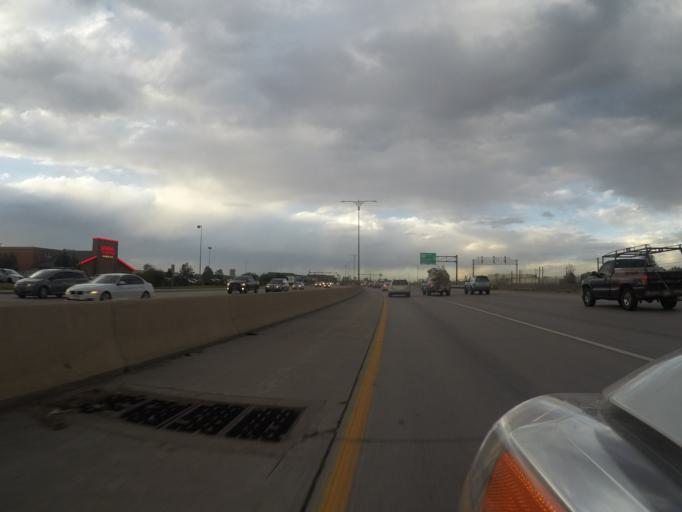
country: US
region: Colorado
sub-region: Arapahoe County
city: Englewood
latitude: 39.6501
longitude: -105.0029
